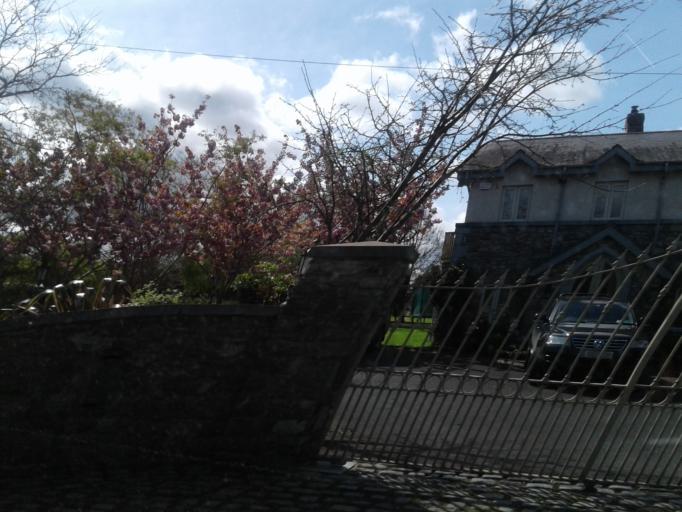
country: IE
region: Leinster
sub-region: Fingal County
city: Swords
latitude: 53.4727
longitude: -6.2544
